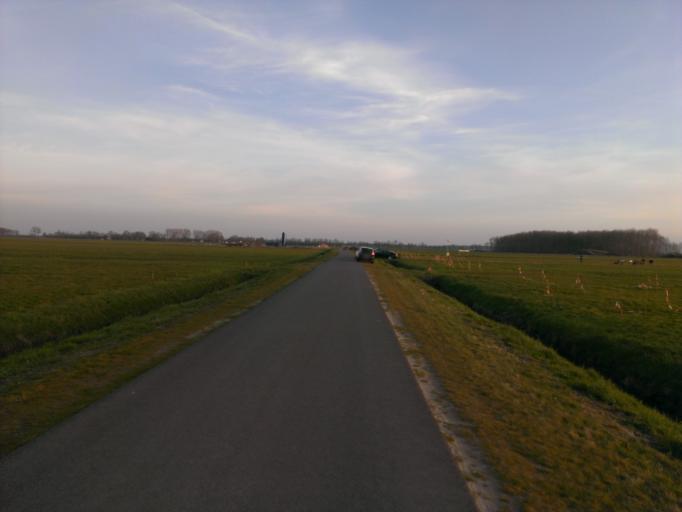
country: NL
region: Overijssel
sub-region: Gemeente Olst-Wijhe
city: Wijhe
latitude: 52.4046
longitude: 6.0938
